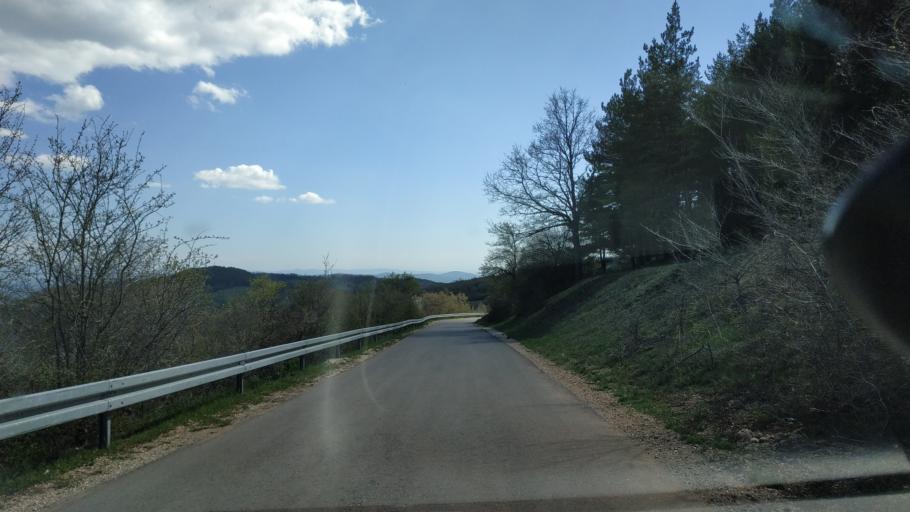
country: RS
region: Central Serbia
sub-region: Zajecarski Okrug
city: Soko Banja
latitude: 43.5791
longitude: 21.8952
